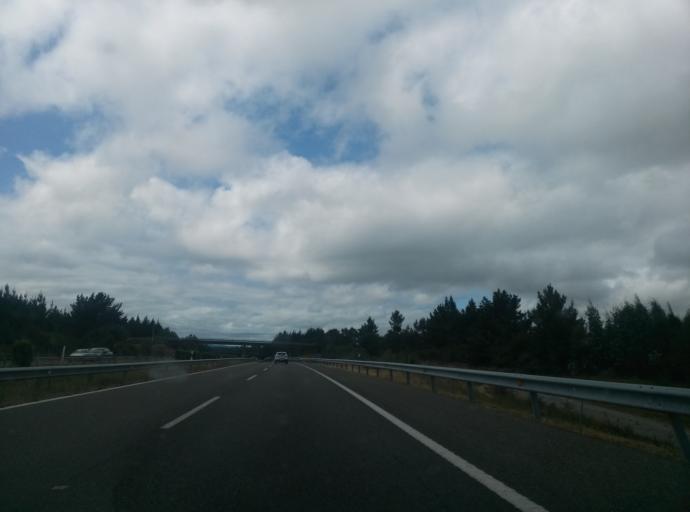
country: ES
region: Galicia
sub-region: Provincia de Lugo
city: Outeiro de Rei
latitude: 43.0903
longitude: -7.5859
